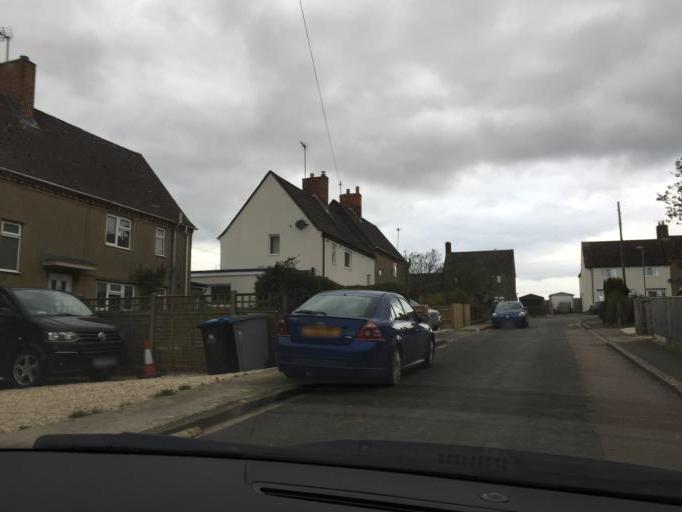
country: GB
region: England
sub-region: Oxfordshire
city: Chipping Norton
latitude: 51.9531
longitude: -1.5445
